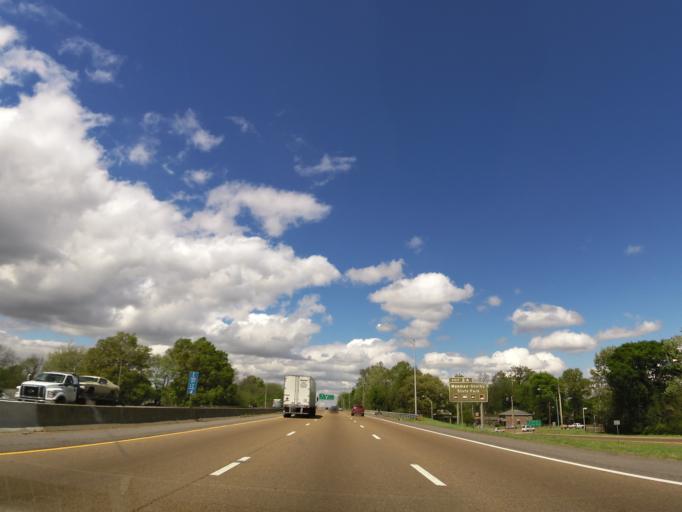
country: US
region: Tennessee
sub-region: Shelby County
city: Memphis
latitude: 35.1691
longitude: -90.0184
